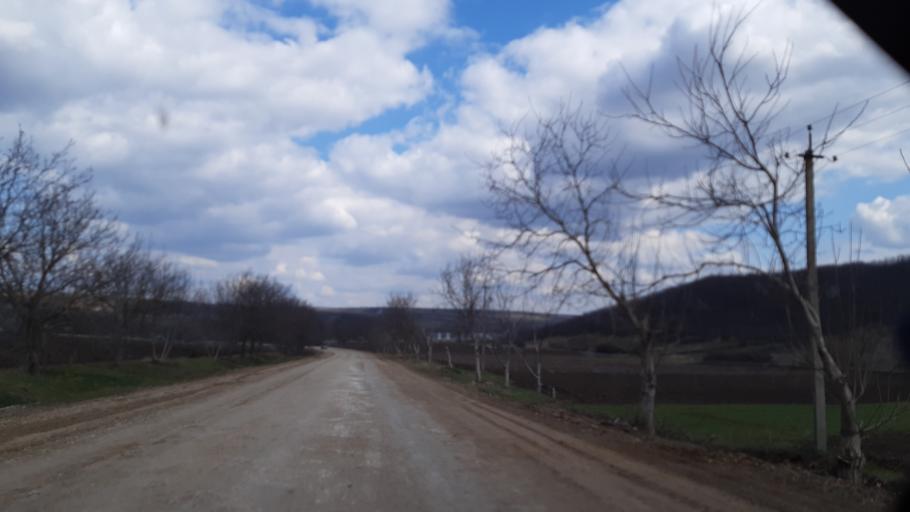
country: MD
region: Laloveni
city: Ialoveni
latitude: 46.8900
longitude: 28.7192
